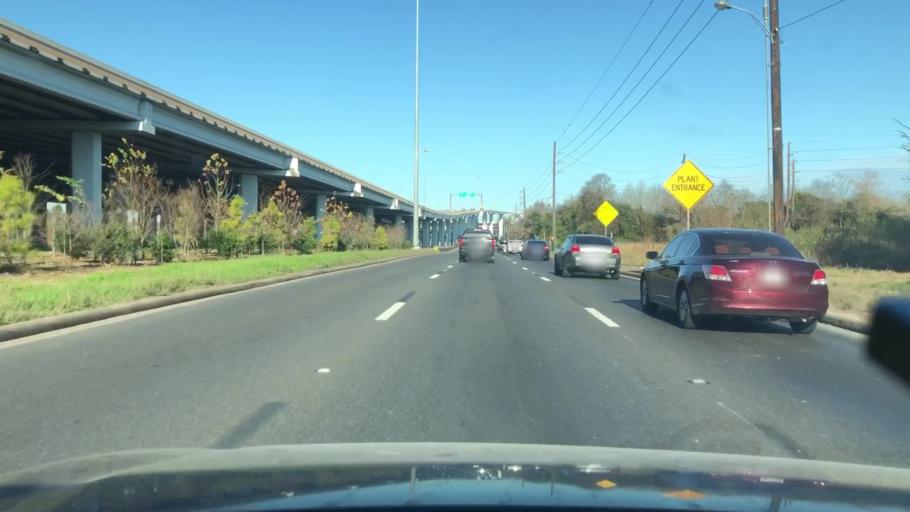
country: US
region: Texas
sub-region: Fort Bend County
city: Meadows Place
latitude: 29.6553
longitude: -95.5515
